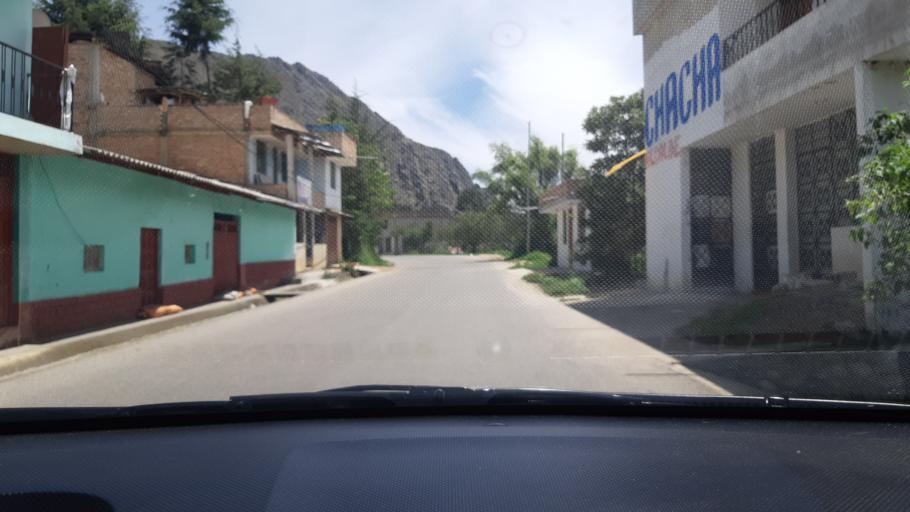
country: PE
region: Cajamarca
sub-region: Provincia de Cajamarca
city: Llacanora
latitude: -7.1818
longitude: -78.4528
